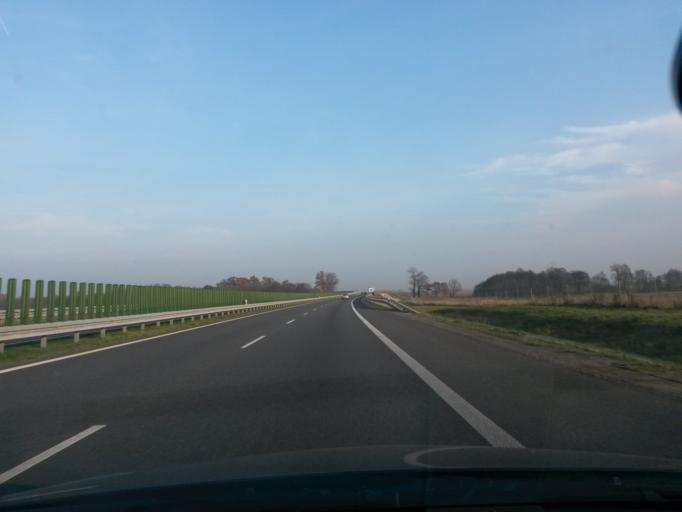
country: PL
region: Lower Silesian Voivodeship
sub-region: Powiat olesnicki
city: Miedzyborz
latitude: 51.3057
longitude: 17.6125
